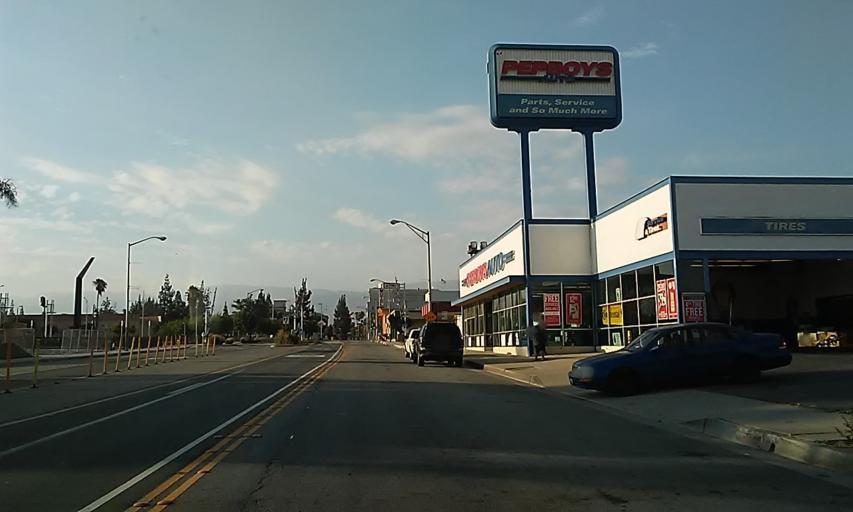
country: US
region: California
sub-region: San Bernardino County
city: San Bernardino
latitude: 34.0989
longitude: -117.2941
